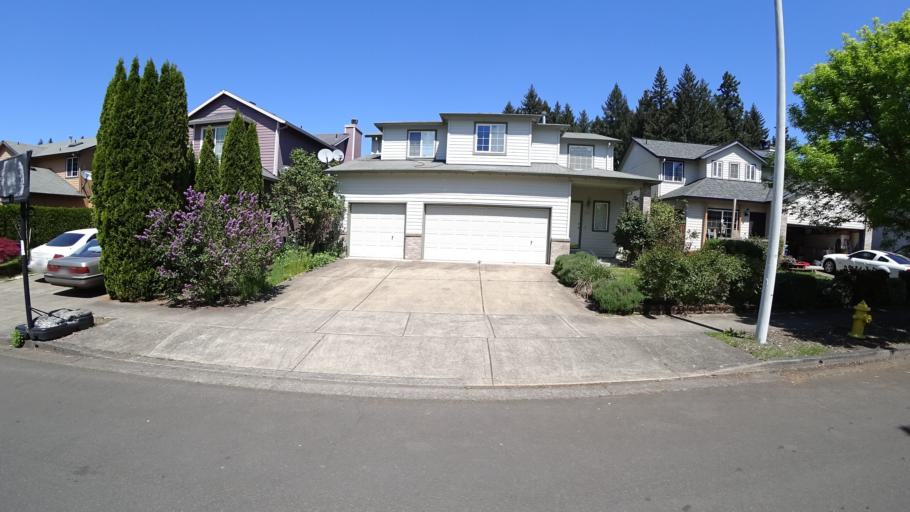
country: US
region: Oregon
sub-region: Washington County
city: Rockcreek
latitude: 45.5183
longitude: -122.9028
